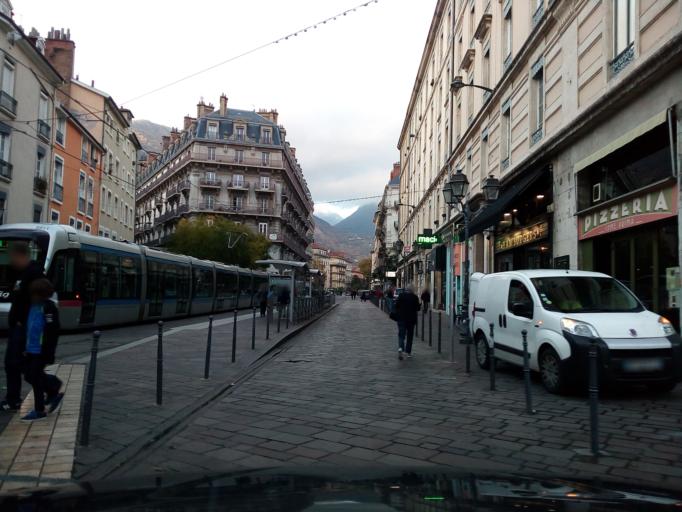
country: FR
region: Rhone-Alpes
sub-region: Departement de l'Isere
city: La Tronche
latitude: 45.1909
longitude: 5.7305
